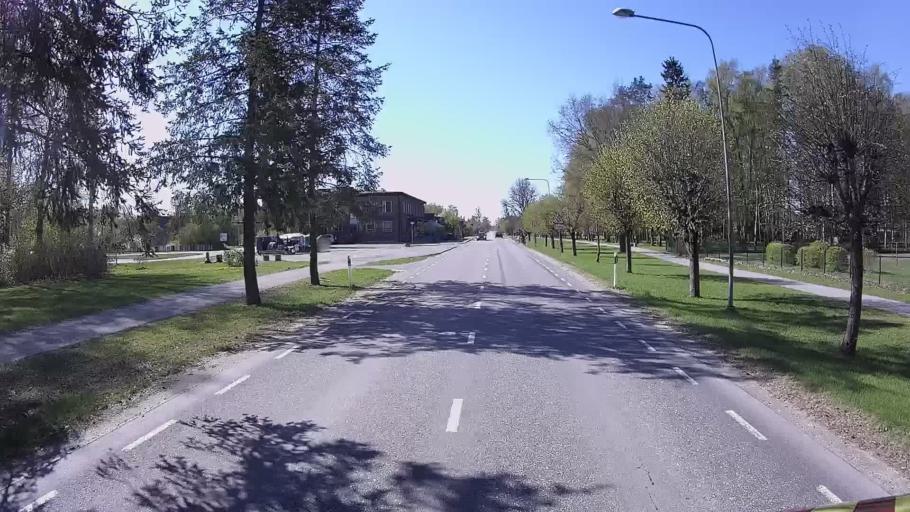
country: EE
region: Raplamaa
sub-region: Jaervakandi vald
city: Jarvakandi
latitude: 58.7749
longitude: 24.8164
